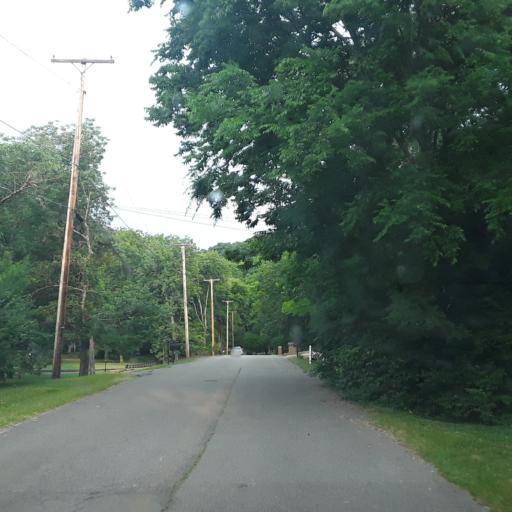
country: US
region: Tennessee
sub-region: Williamson County
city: Brentwood
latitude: 36.0598
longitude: -86.7757
